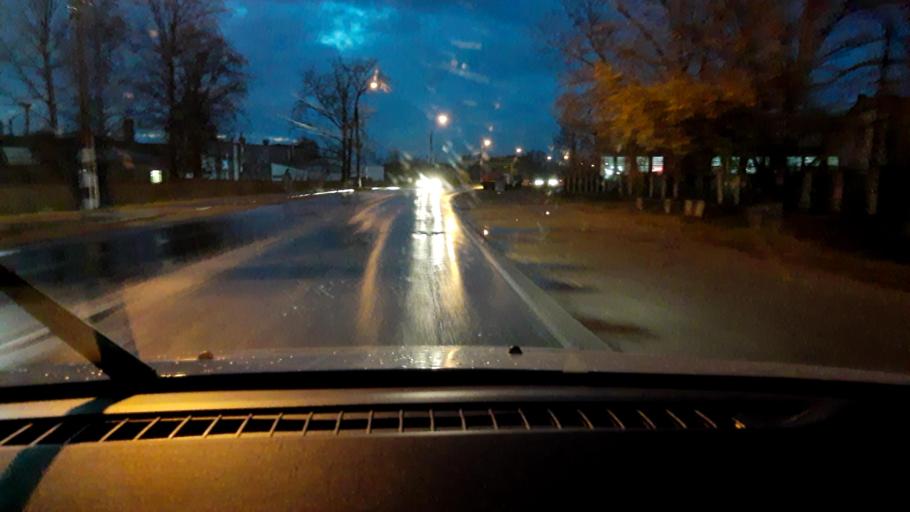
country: RU
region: Nizjnij Novgorod
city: Bor
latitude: 56.3474
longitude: 44.0826
